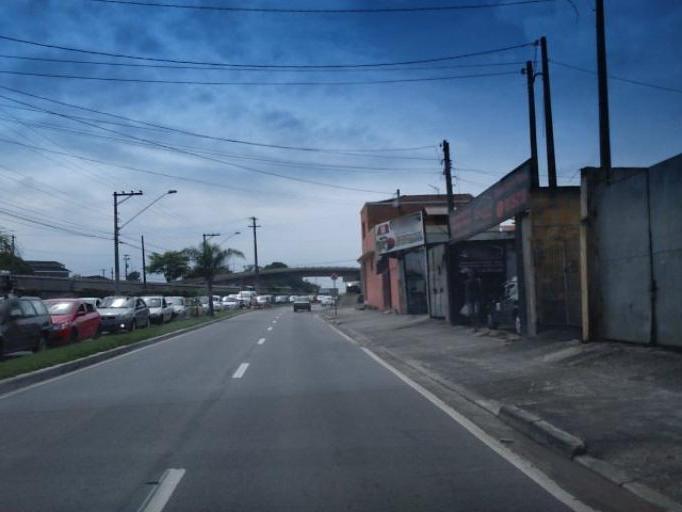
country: BR
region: Sao Paulo
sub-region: Sao Jose Dos Campos
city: Sao Jose dos Campos
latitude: -23.1739
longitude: -45.8807
